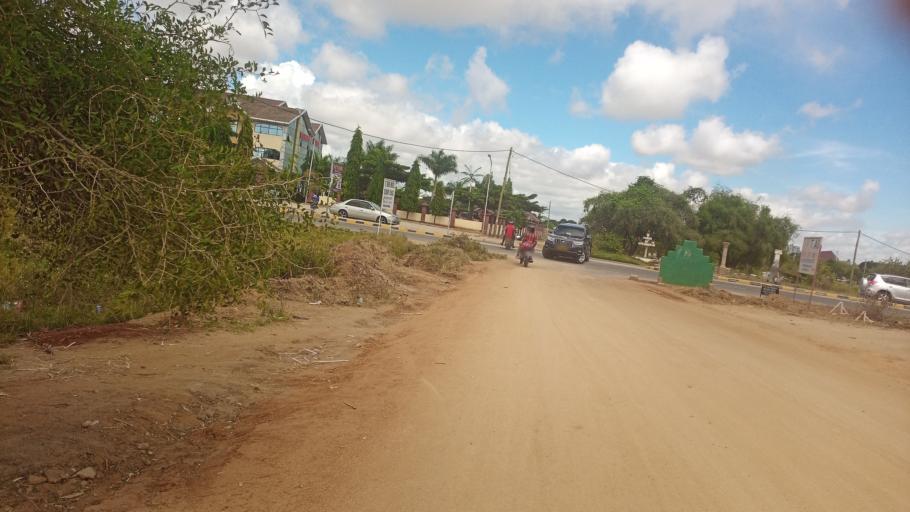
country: TZ
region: Dodoma
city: Dodoma
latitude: -6.1759
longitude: 35.7640
